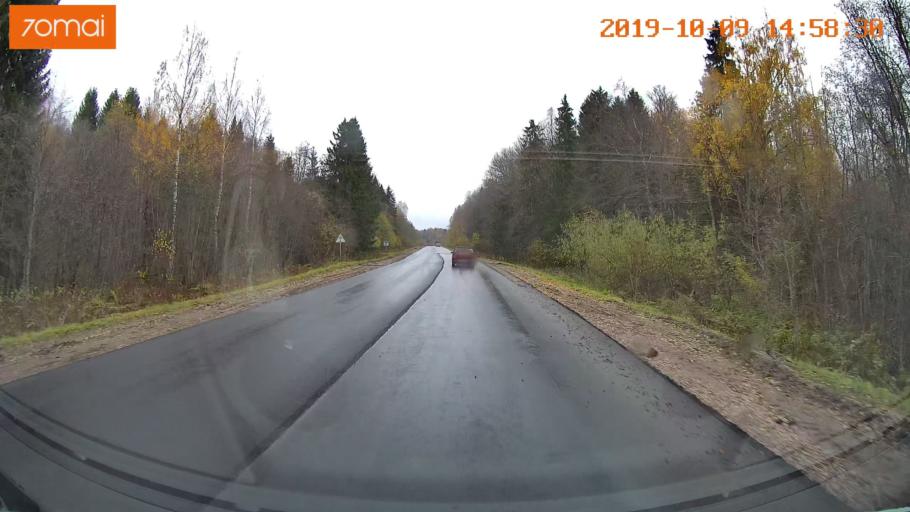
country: RU
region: Kostroma
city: Chistyye Bory
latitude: 58.3262
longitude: 41.6555
